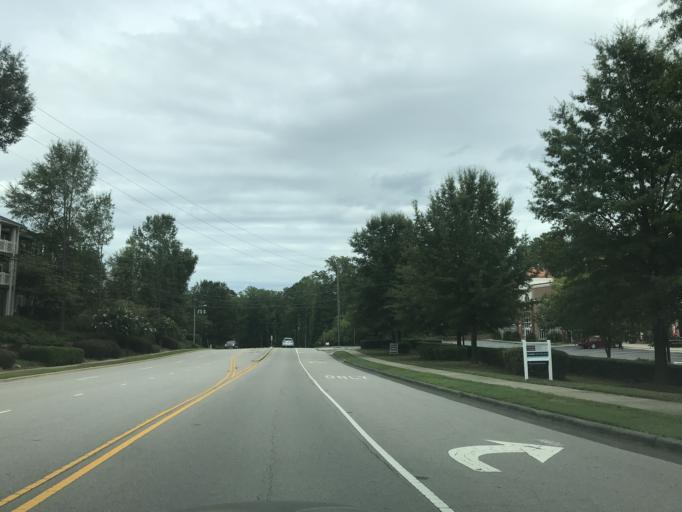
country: US
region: North Carolina
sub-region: Wake County
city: Apex
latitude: 35.7457
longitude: -78.8193
